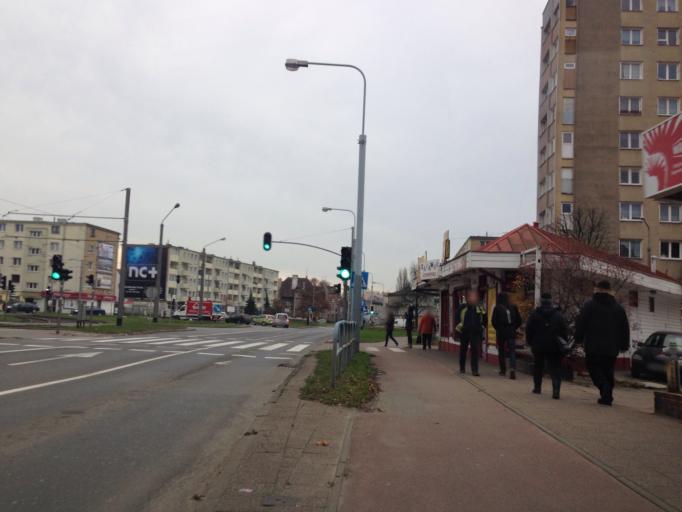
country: PL
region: Pomeranian Voivodeship
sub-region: Gdansk
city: Gdansk
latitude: 54.3837
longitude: 18.6138
